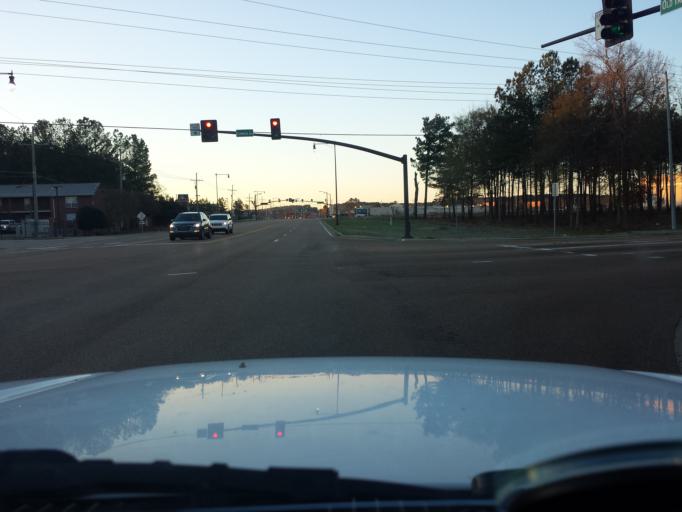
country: US
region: Mississippi
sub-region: Rankin County
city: Flowood
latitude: 32.3456
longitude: -90.0648
